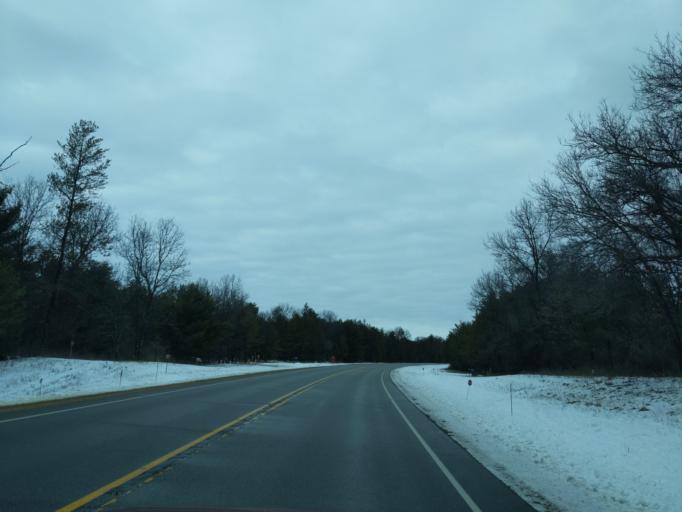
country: US
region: Wisconsin
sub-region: Waushara County
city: Wautoma
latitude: 43.9665
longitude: -89.3269
